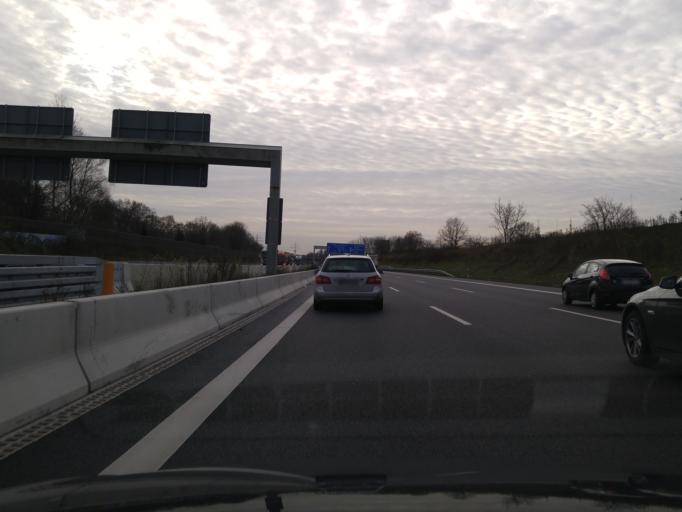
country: DE
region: Schleswig-Holstein
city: Oststeinbek
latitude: 53.5537
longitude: 10.1512
